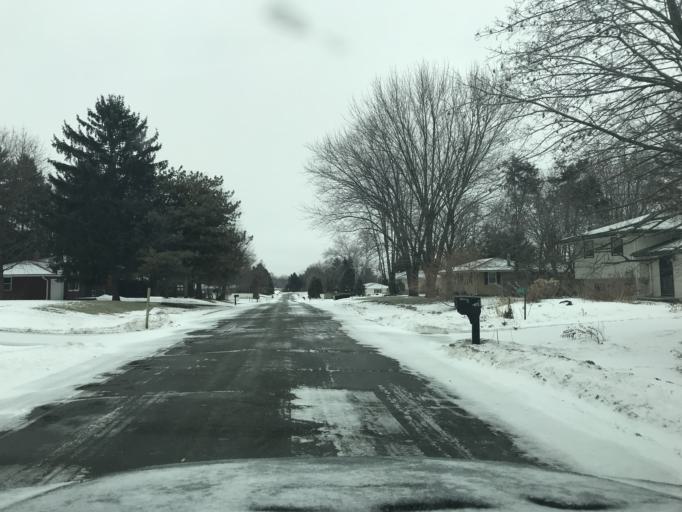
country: US
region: Wisconsin
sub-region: Dane County
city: Cottage Grove
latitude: 43.0966
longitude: -89.2363
